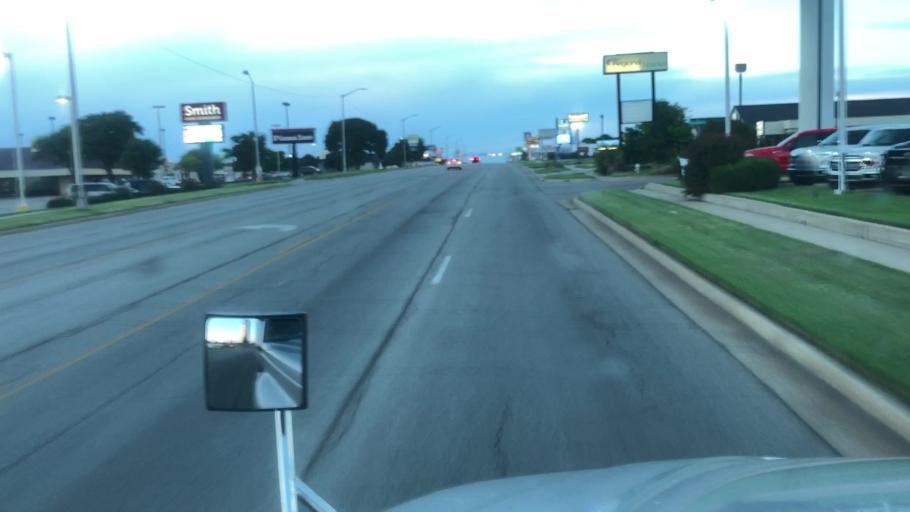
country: US
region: Oklahoma
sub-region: Kay County
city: Ponca City
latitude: 36.7339
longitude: -97.0672
